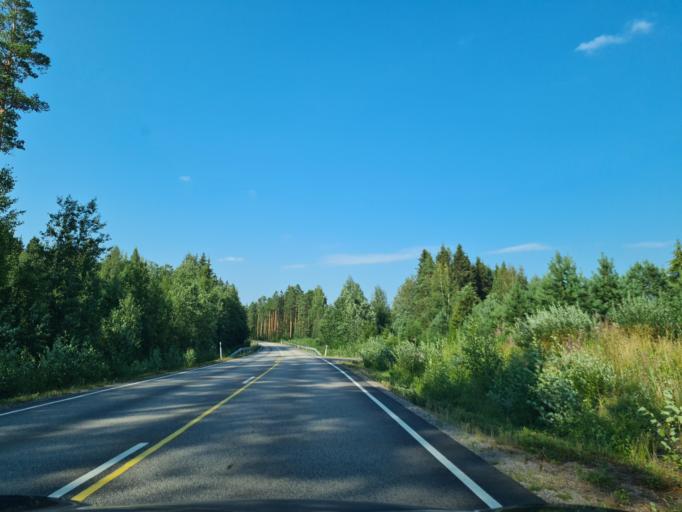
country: FI
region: Satakunta
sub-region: Pohjois-Satakunta
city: Karvia
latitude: 62.2244
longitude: 22.6147
